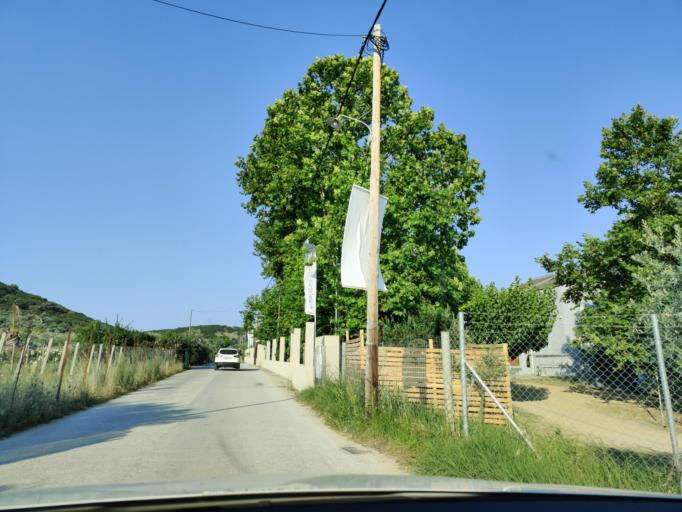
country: GR
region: East Macedonia and Thrace
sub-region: Nomos Kavalas
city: Nea Peramos
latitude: 40.8180
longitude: 24.3027
